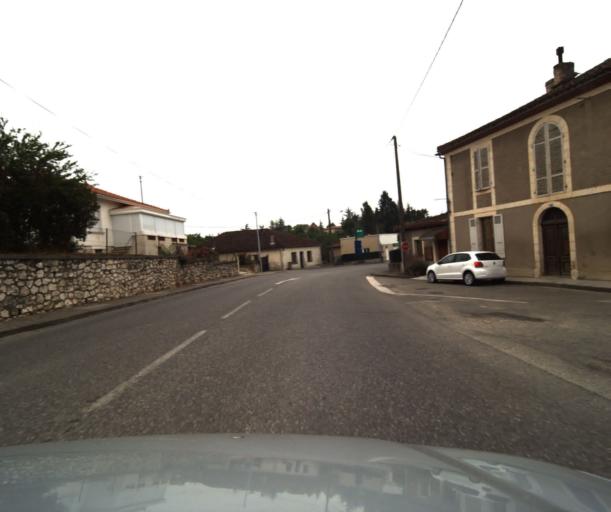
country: FR
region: Midi-Pyrenees
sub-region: Departement du Gers
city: Gimont
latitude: 43.7286
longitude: 0.8778
